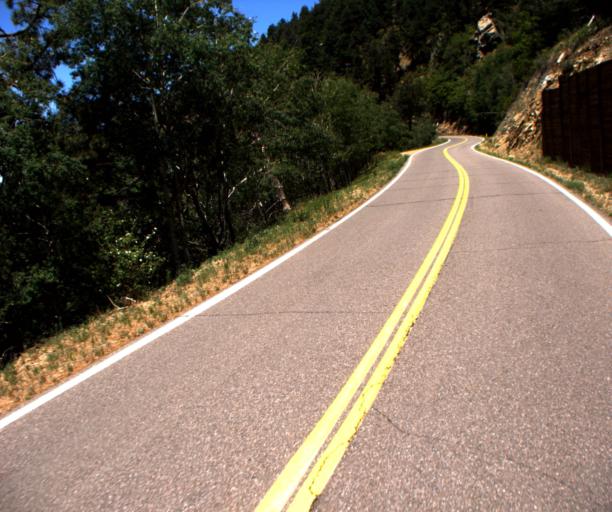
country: US
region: Arizona
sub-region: Graham County
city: Swift Trail Junction
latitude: 32.6476
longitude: -109.8578
